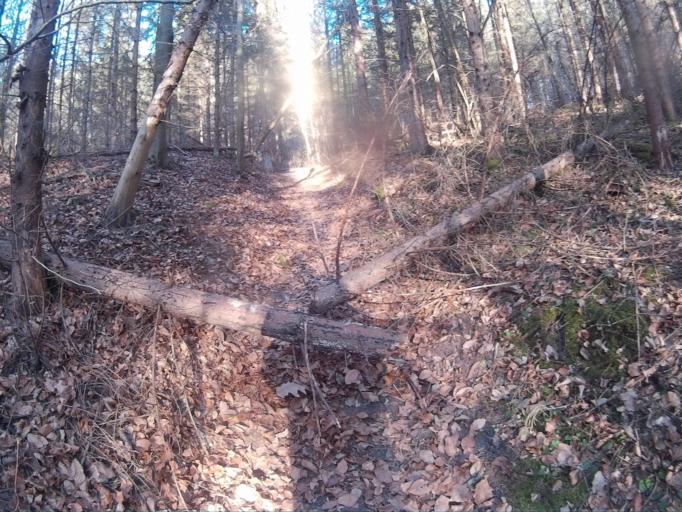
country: HU
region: Borsod-Abauj-Zemplen
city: Rudabanya
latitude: 48.5328
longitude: 20.6264
